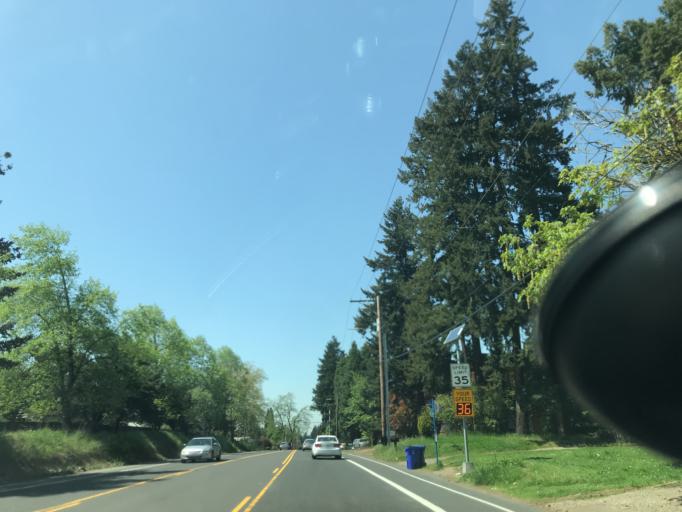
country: US
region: Oregon
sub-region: Multnomah County
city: Gresham
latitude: 45.4935
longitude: -122.4901
